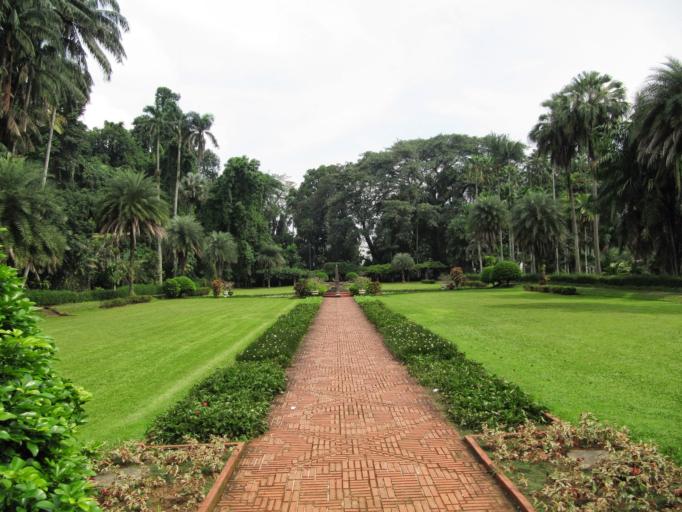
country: ID
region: West Java
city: Bogor
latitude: -6.6004
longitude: 106.7961
